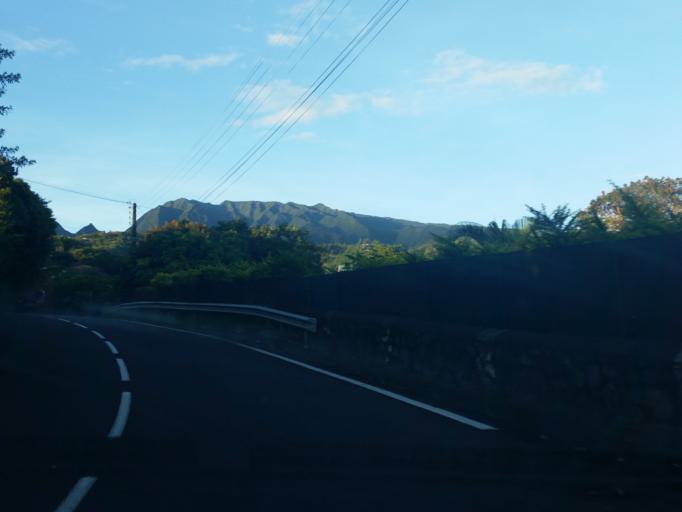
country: RE
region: Reunion
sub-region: Reunion
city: L'Entre-Deux
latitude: -21.2444
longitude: 55.4811
